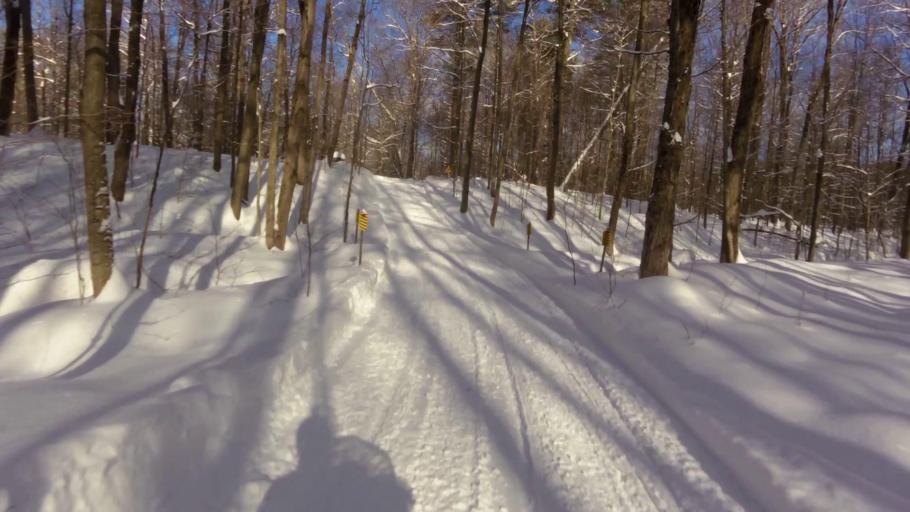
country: US
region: New York
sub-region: Chautauqua County
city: Falconer
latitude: 42.2596
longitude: -79.1448
